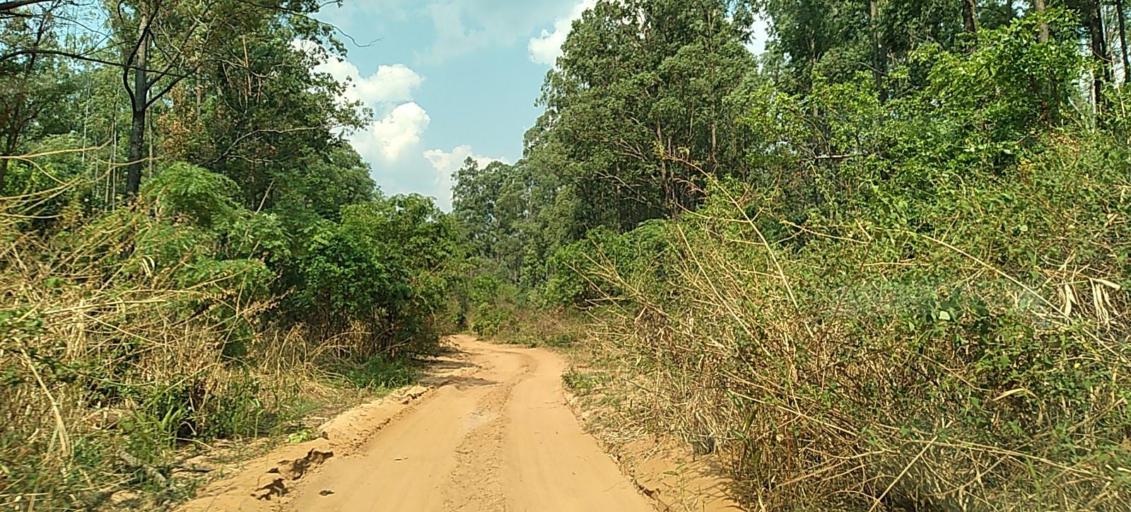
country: ZM
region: Copperbelt
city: Chingola
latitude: -12.7395
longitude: 27.7633
